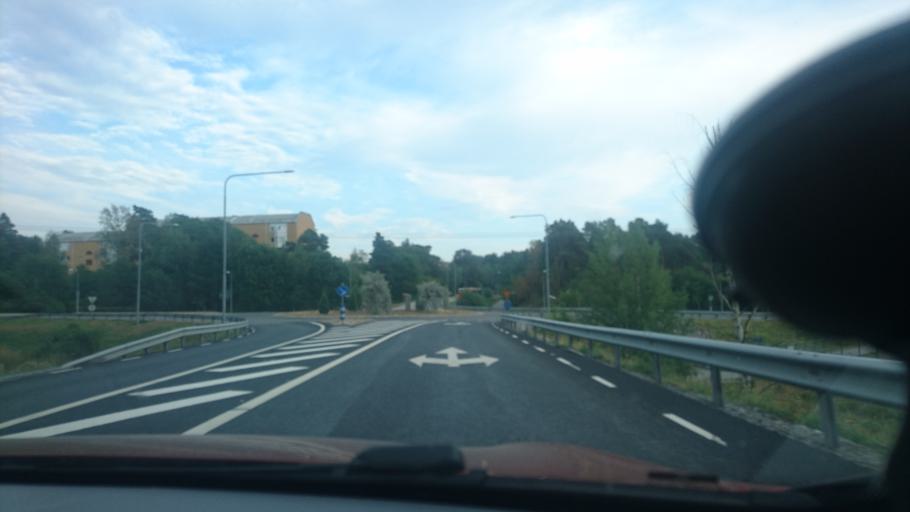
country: SE
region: Stockholm
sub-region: Upplands Vasby Kommun
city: Upplands Vaesby
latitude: 59.4989
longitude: 17.9318
